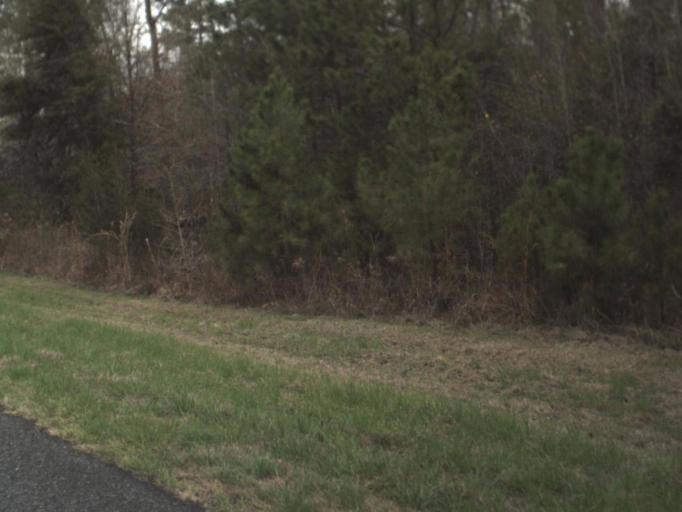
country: US
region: Florida
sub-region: Leon County
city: Woodville
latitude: 30.4029
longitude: -84.0535
